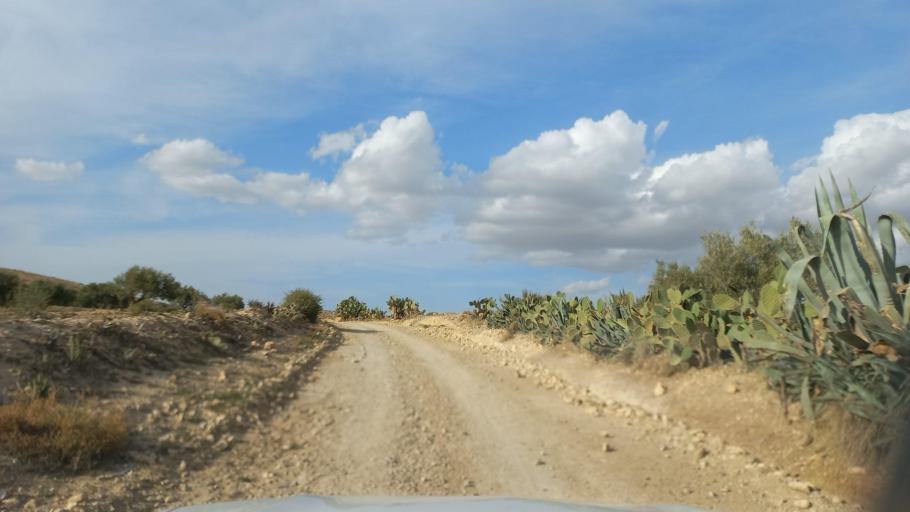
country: TN
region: Al Qasrayn
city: Sbiba
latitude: 35.4547
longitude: 9.0836
